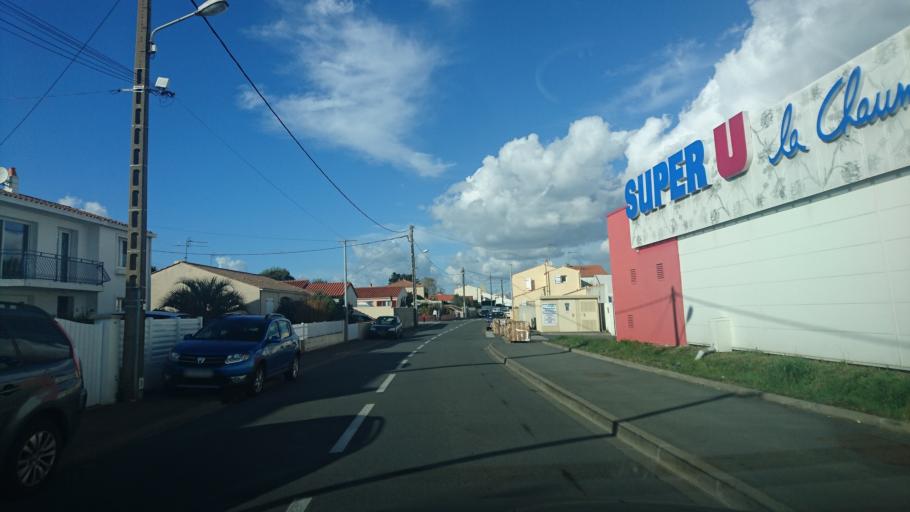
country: FR
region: Pays de la Loire
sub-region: Departement de la Vendee
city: Les Sables-d'Olonne
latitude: 46.5038
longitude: -1.7998
